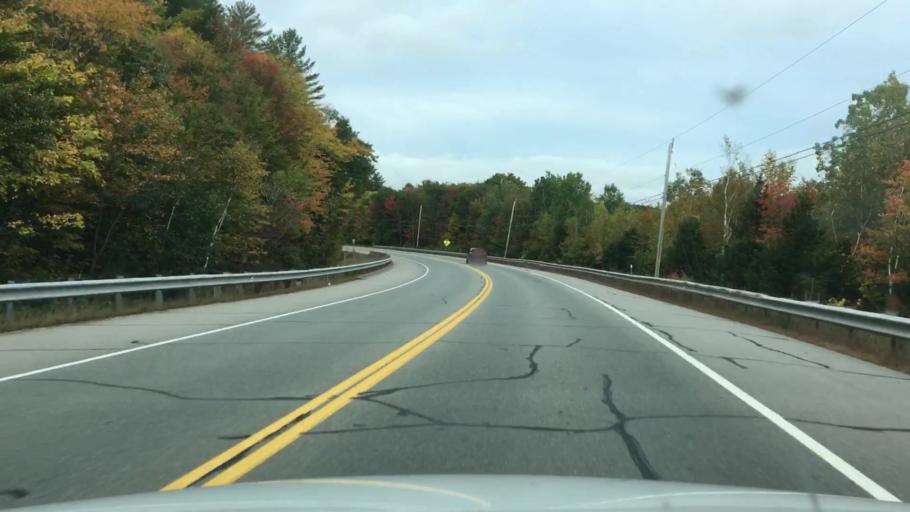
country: US
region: New Hampshire
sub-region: Coos County
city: Gorham
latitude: 44.3978
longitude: -71.0564
